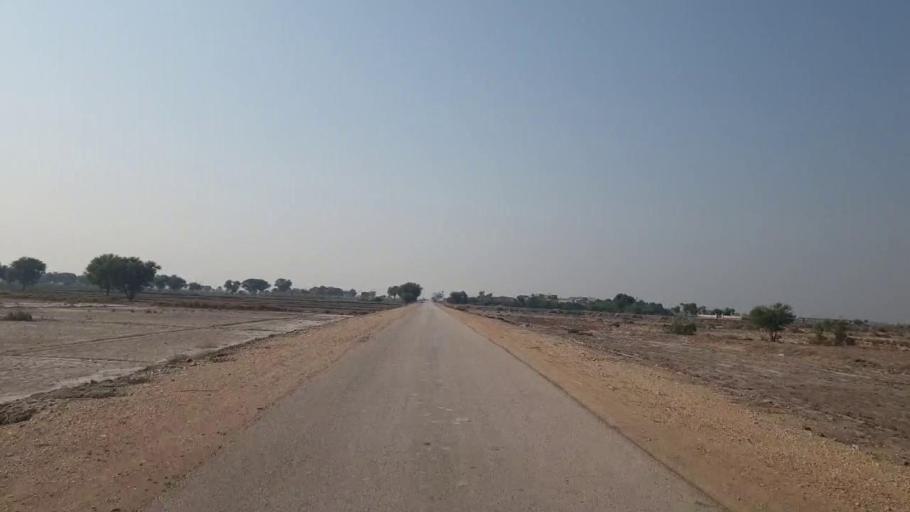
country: PK
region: Sindh
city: Sehwan
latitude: 26.4258
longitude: 67.8333
